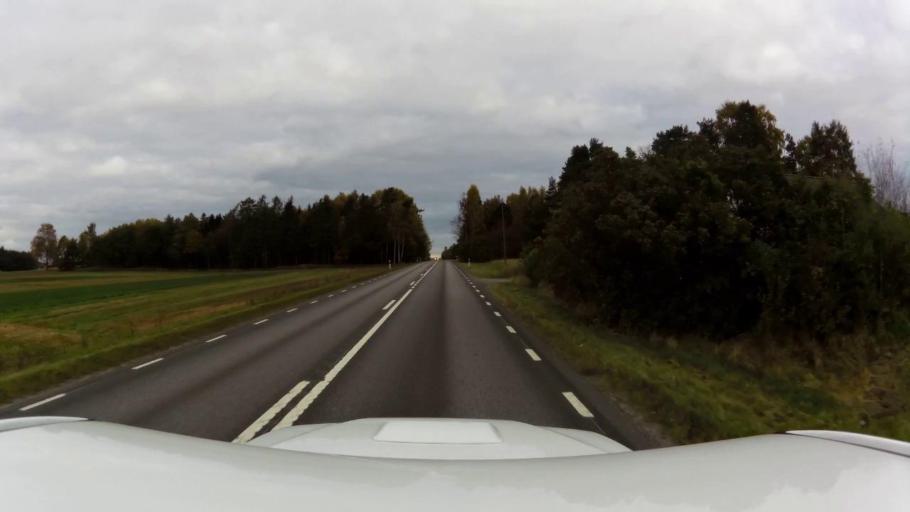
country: SE
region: OEstergoetland
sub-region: Linkopings Kommun
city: Ljungsbro
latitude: 58.5055
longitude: 15.4513
